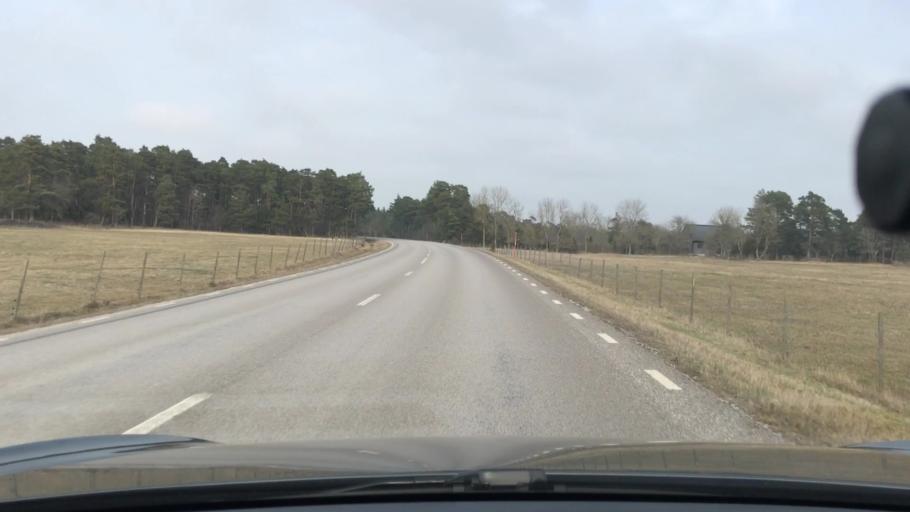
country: SE
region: Gotland
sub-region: Gotland
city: Slite
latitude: 57.4360
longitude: 18.6906
